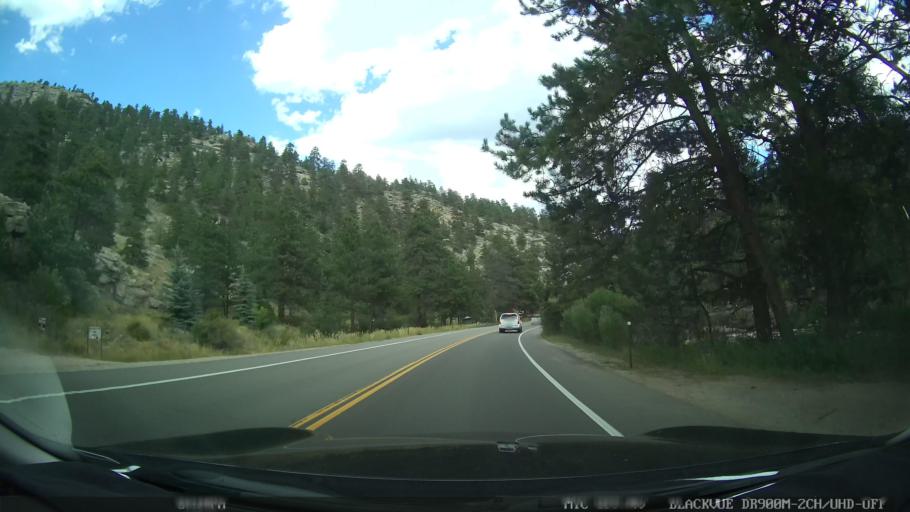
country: US
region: Colorado
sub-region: Larimer County
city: Estes Park
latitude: 40.3800
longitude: -105.4777
